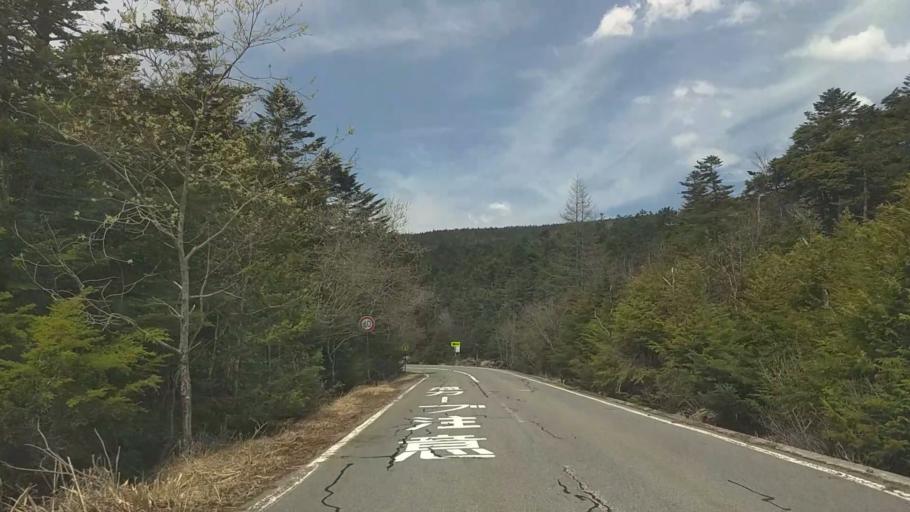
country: JP
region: Nagano
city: Chino
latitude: 36.0580
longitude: 138.3288
